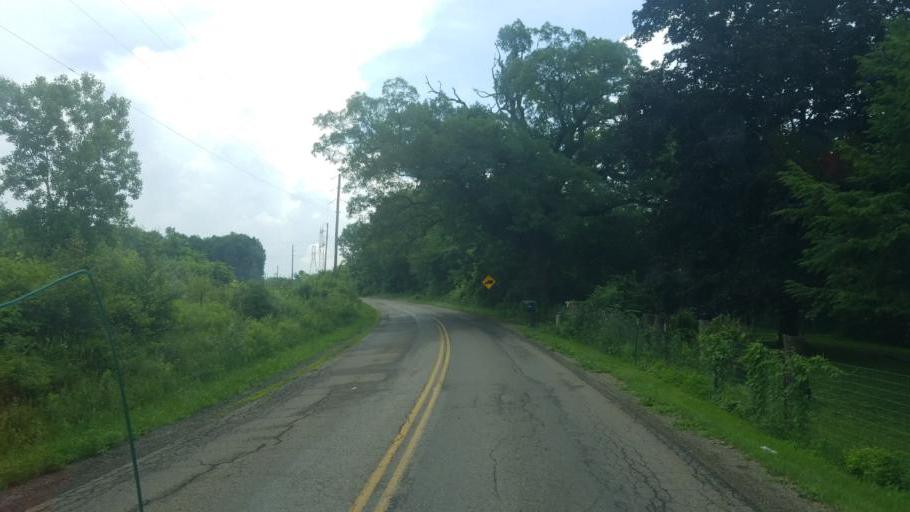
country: US
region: Ohio
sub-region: Summit County
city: Clinton
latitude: 40.8952
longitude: -81.6579
